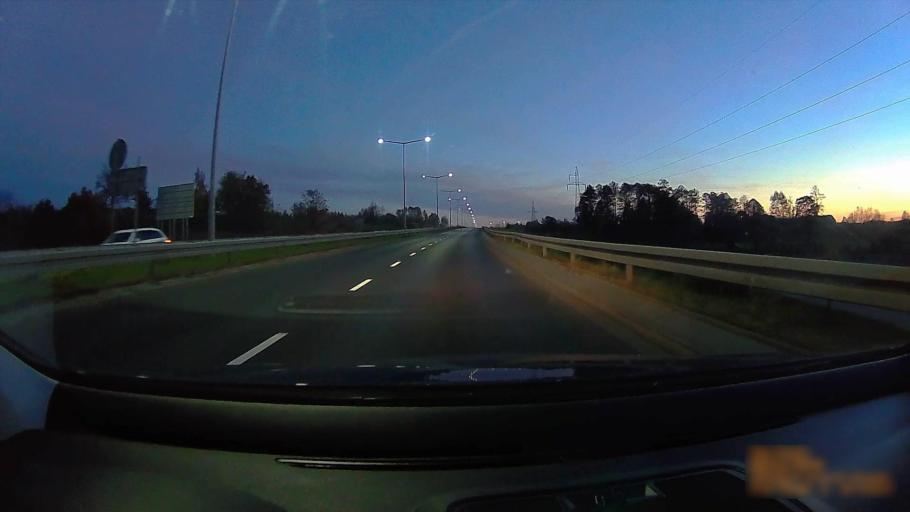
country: PL
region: Greater Poland Voivodeship
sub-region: Powiat koninski
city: Stare Miasto
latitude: 52.2027
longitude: 18.2255
